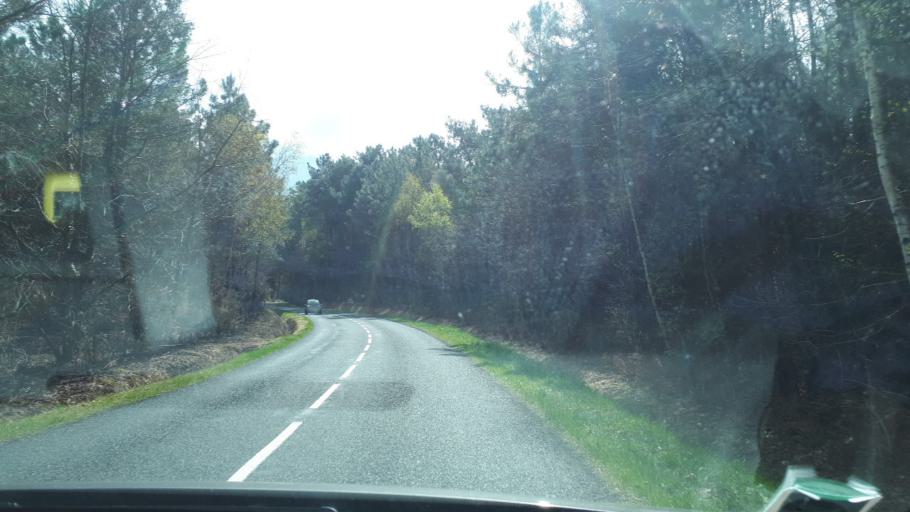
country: FR
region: Pays de la Loire
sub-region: Departement de la Sarthe
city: Brette-les-Pins
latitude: 47.8662
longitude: 0.3573
